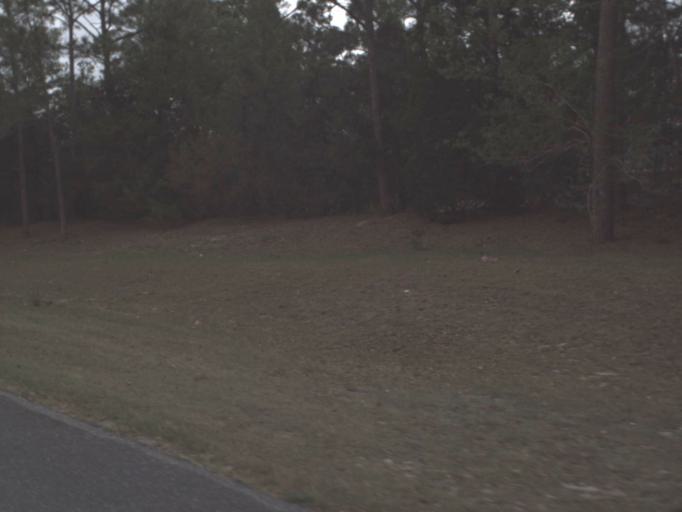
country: US
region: Florida
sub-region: Marion County
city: Ocala
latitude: 29.2371
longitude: -82.0488
